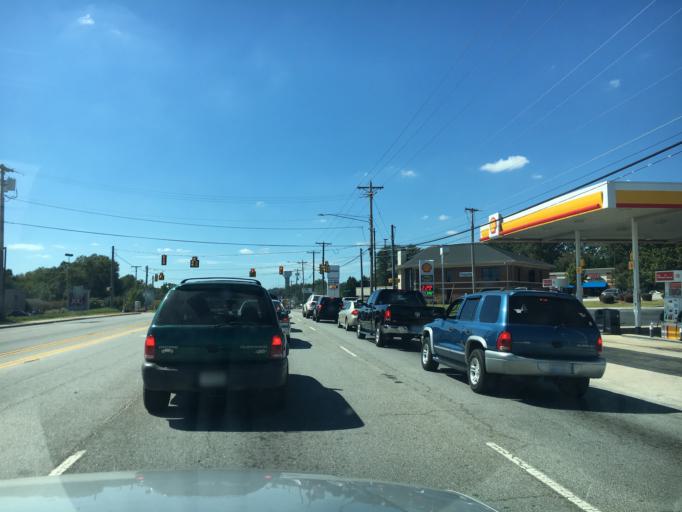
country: US
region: South Carolina
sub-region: Pickens County
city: Easley
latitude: 34.8219
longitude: -82.5866
